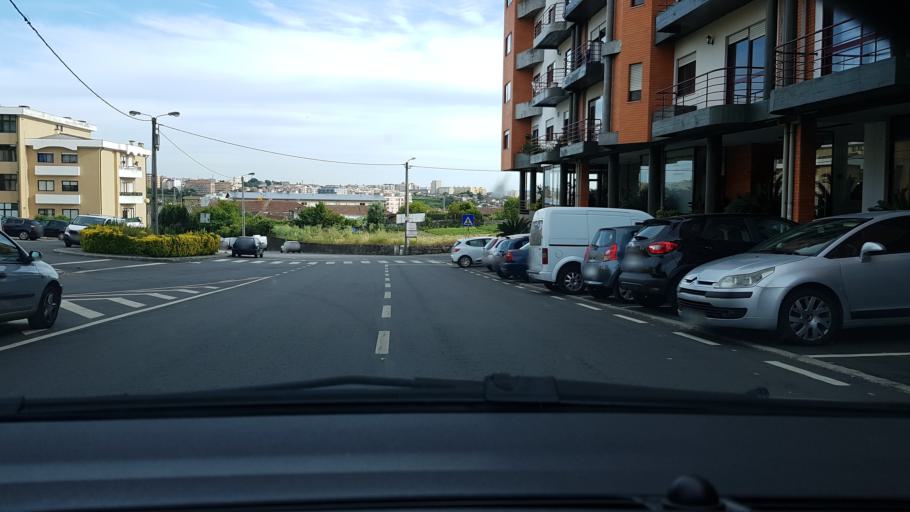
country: PT
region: Porto
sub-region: Gondomar
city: Rio Tinto
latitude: 41.1889
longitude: -8.5541
